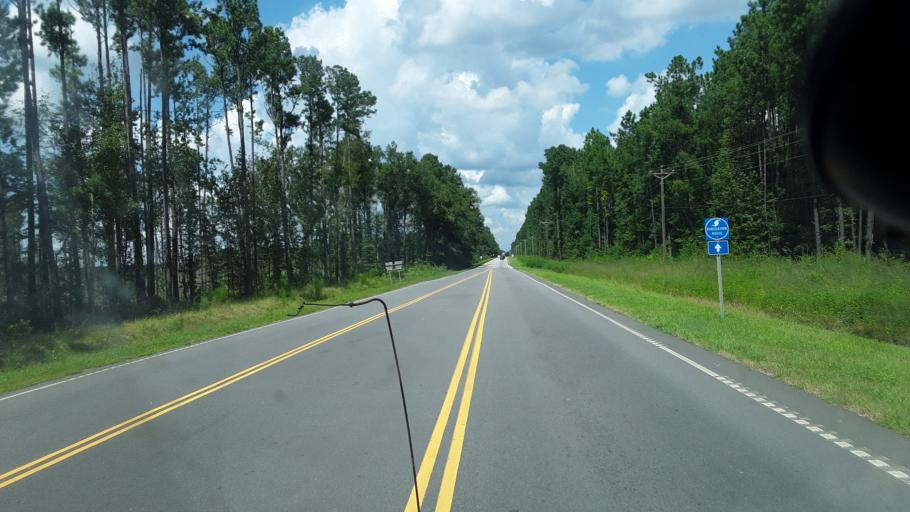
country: US
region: South Carolina
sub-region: Williamsburg County
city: Andrews
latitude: 33.5970
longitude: -79.4423
